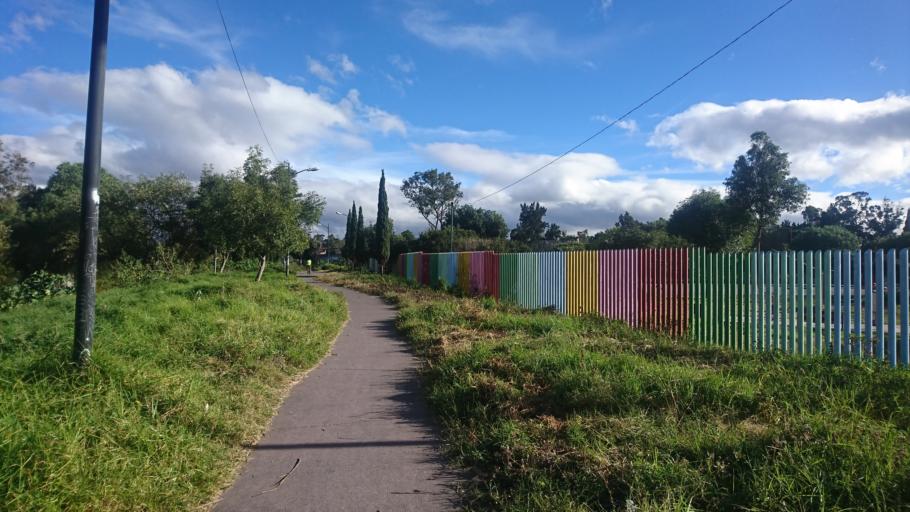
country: MX
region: Mexico City
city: Iztapalapa
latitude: 19.3257
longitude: -99.1054
